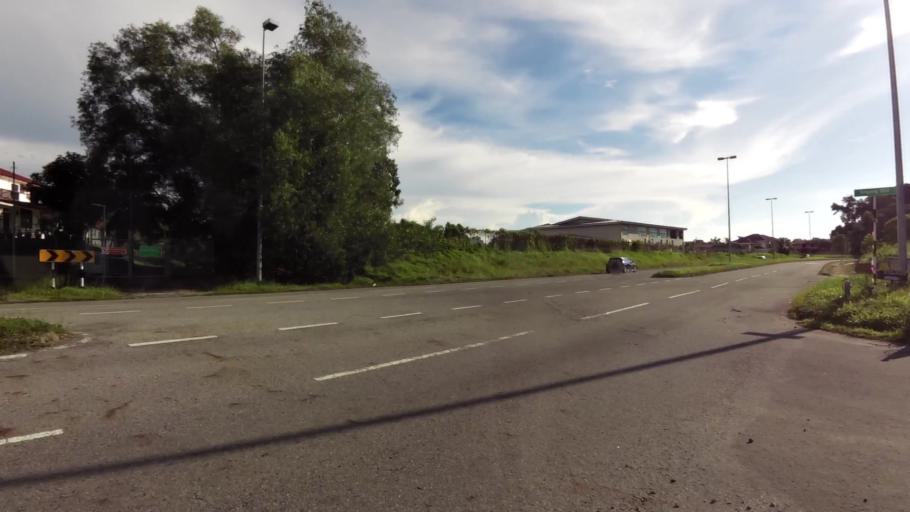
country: BN
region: Brunei and Muara
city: Bandar Seri Begawan
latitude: 4.9809
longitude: 114.9614
